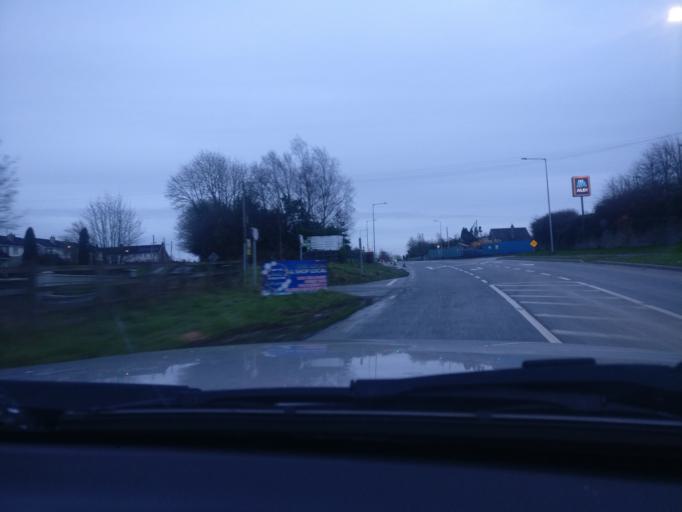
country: IE
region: Leinster
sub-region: An Mhi
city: Kells
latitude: 53.7320
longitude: -6.8903
